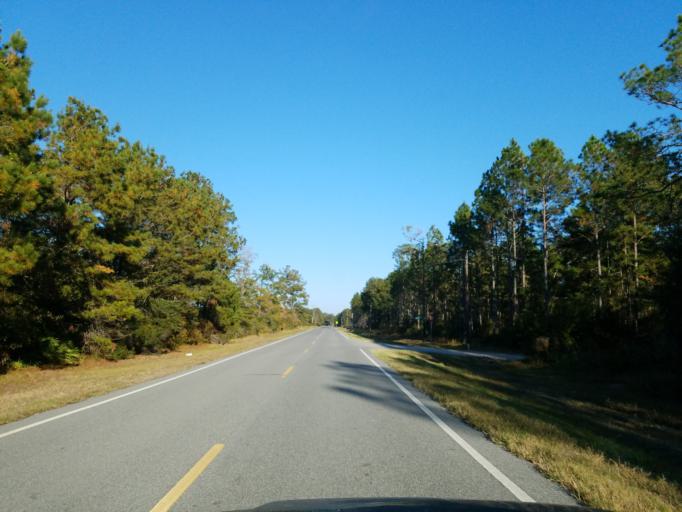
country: US
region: Georgia
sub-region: Echols County
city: Statenville
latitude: 30.6323
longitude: -83.0762
